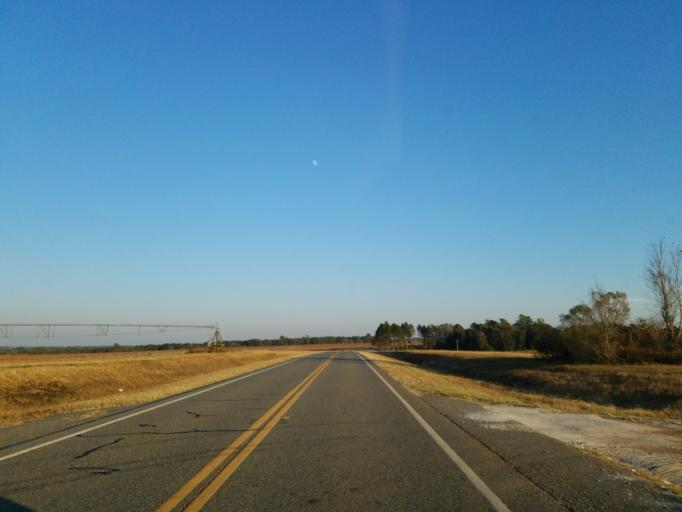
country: US
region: Georgia
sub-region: Turner County
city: Ashburn
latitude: 31.8590
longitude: -83.5964
